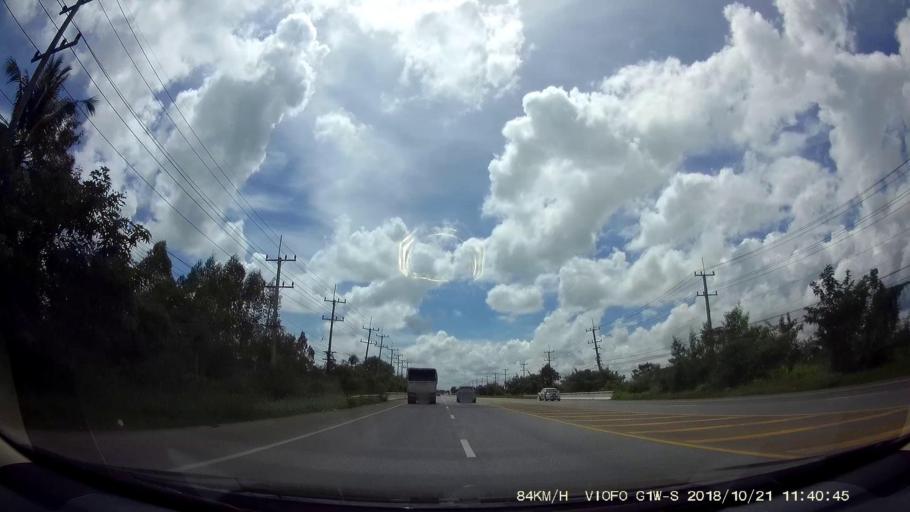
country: TH
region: Chaiyaphum
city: Chaiyaphum
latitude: 15.7094
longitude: 102.0154
